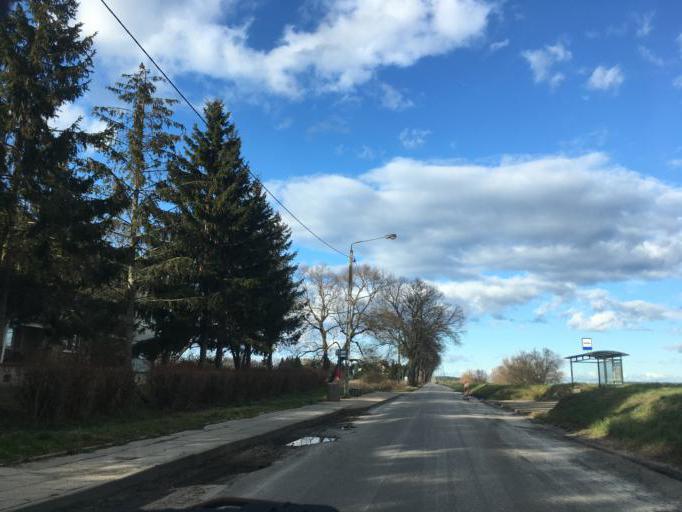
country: PL
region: Pomeranian Voivodeship
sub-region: Powiat nowodworski
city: Ostaszewo
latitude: 54.3146
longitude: 18.9305
